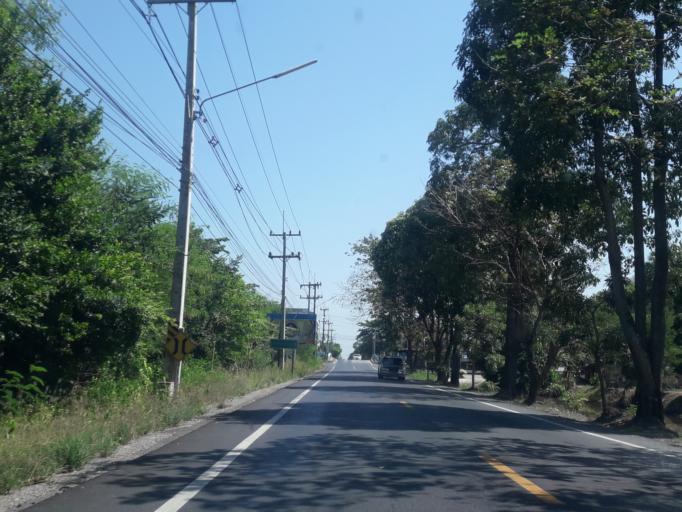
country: TH
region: Pathum Thani
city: Nong Suea
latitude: 14.1368
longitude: 100.8448
